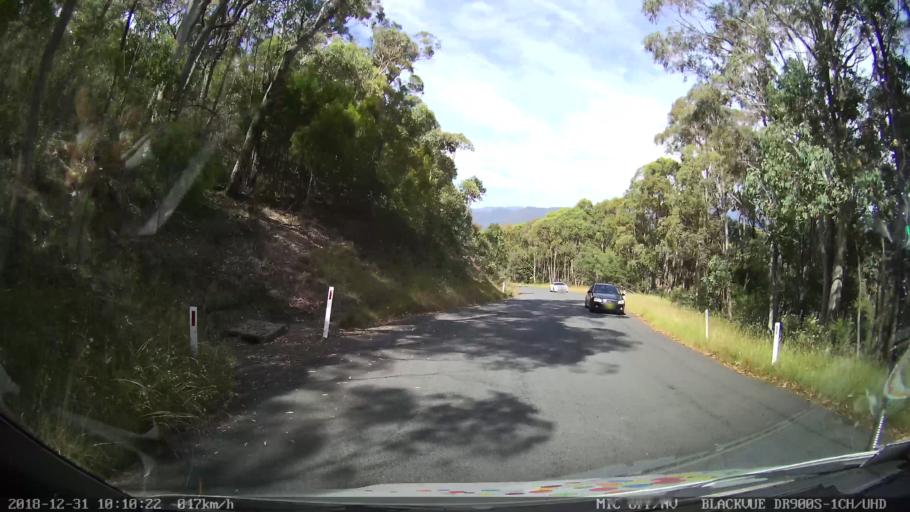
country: AU
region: New South Wales
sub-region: Snowy River
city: Jindabyne
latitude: -36.5364
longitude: 148.1704
